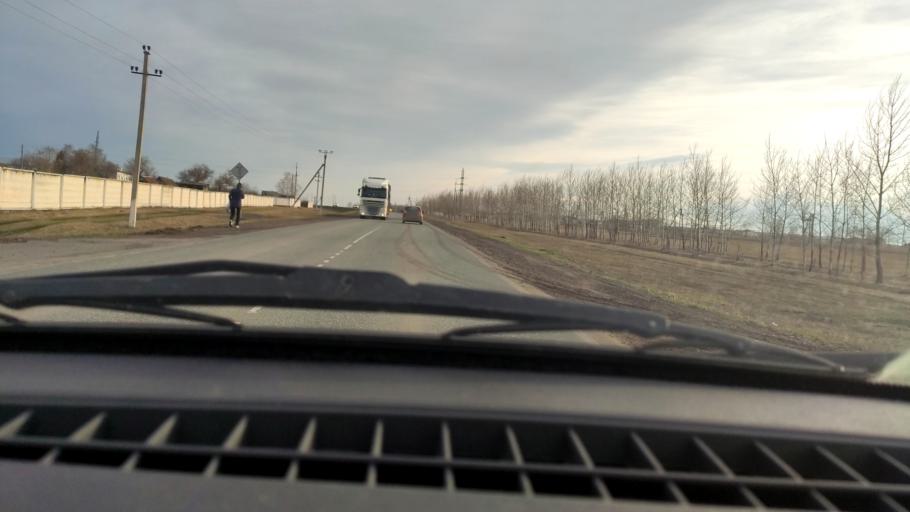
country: RU
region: Bashkortostan
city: Davlekanovo
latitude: 54.3862
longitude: 55.1985
